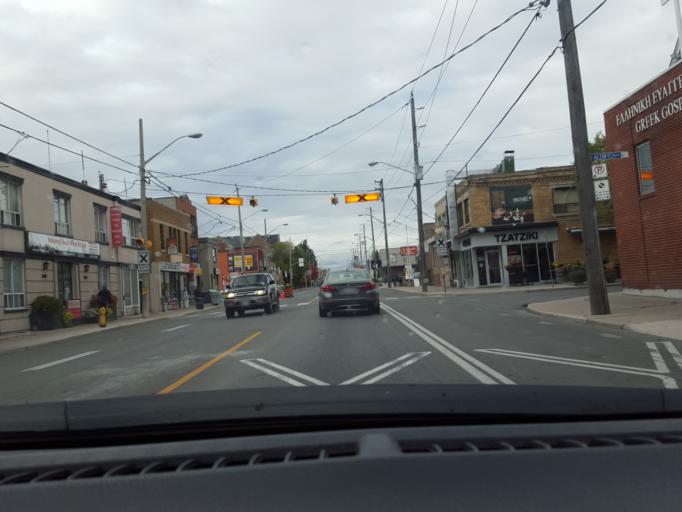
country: CA
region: Ontario
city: Toronto
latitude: 43.6833
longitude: -79.3465
